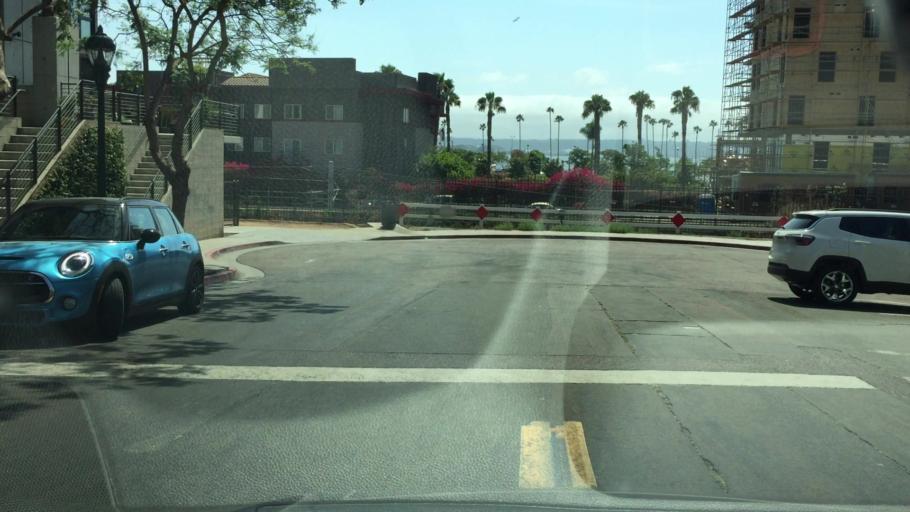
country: US
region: California
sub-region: San Diego County
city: San Diego
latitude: 32.7240
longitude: -117.1698
